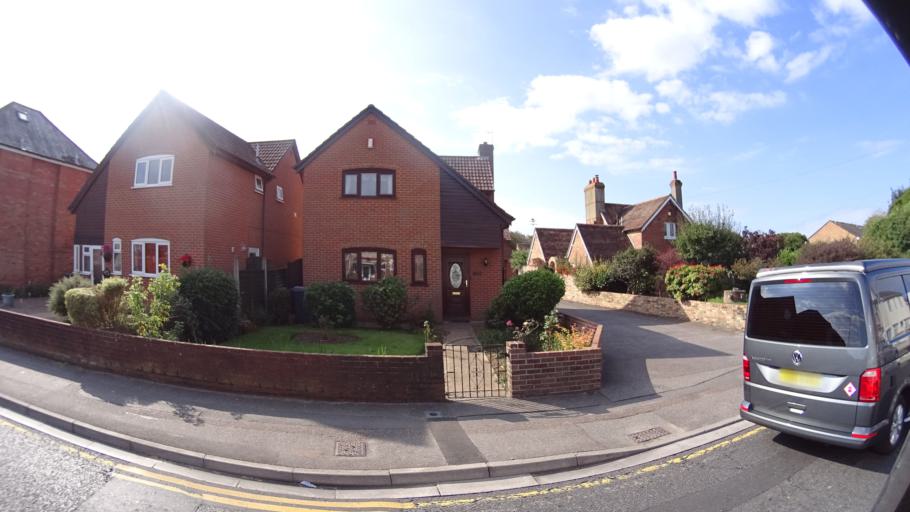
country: GB
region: England
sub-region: Bournemouth
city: Bournemouth
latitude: 50.7520
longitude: -1.8910
